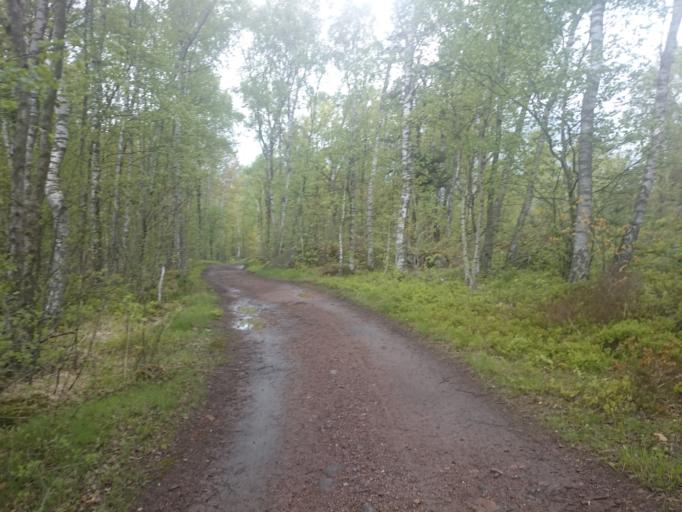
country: SE
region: Vaestra Goetaland
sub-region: Goteborg
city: Goeteborg
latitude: 57.6754
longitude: 11.9584
